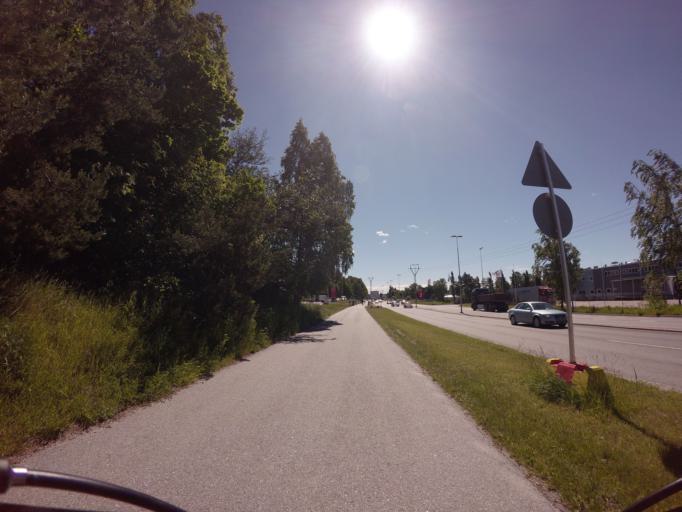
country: FI
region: Varsinais-Suomi
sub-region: Turku
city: Turku
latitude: 60.4471
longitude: 22.2199
